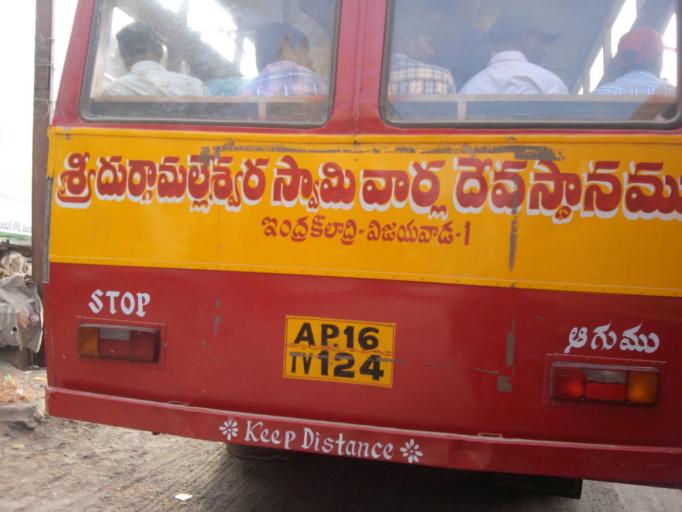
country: IN
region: Andhra Pradesh
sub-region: Krishna
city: Vijayawada
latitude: 16.5131
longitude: 80.6038
